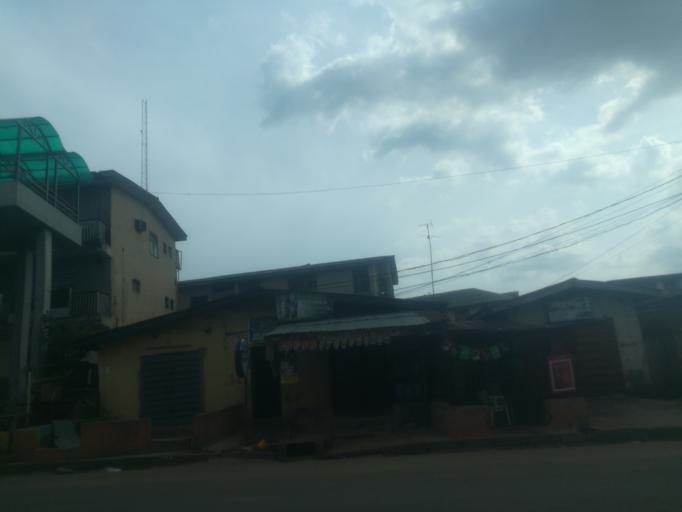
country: NG
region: Ogun
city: Abeokuta
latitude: 7.1357
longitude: 3.3311
